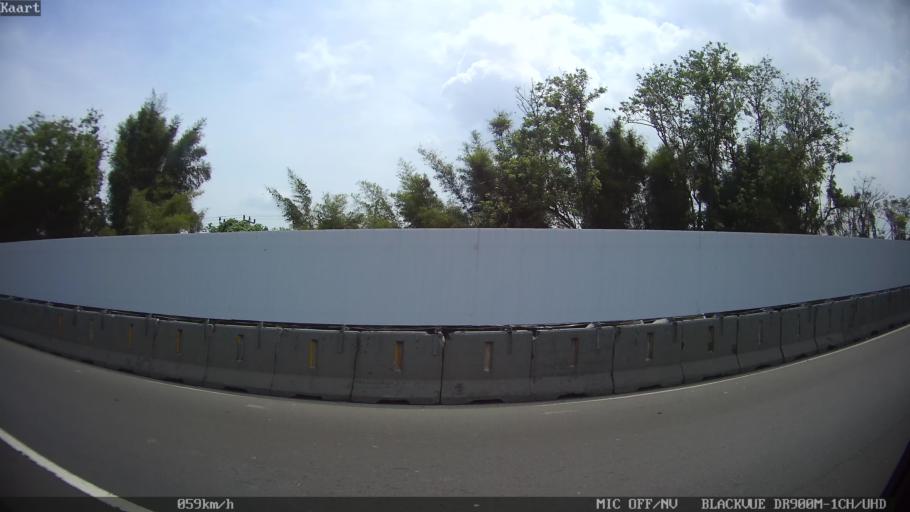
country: ID
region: Banten
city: Serang
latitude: -6.1261
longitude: 106.1918
